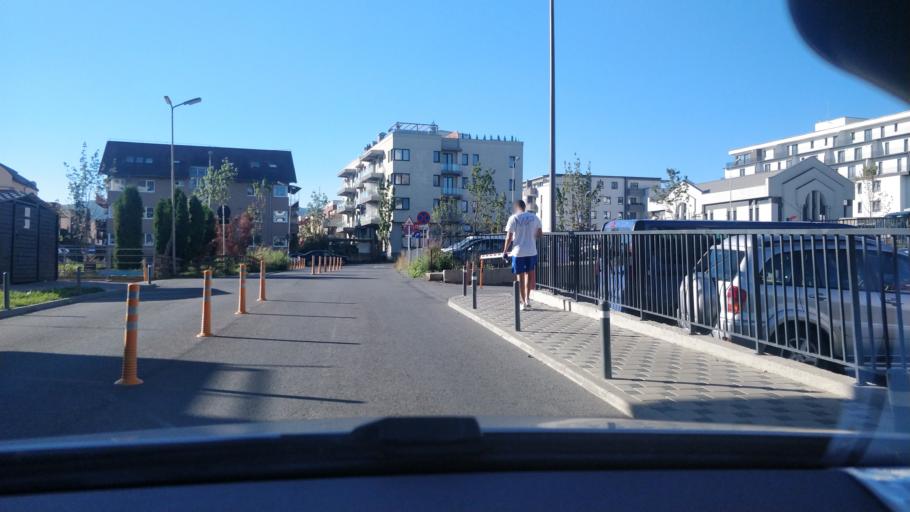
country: RO
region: Cluj
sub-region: Municipiul Cluj-Napoca
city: Cluj-Napoca
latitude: 46.7496
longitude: 23.6013
